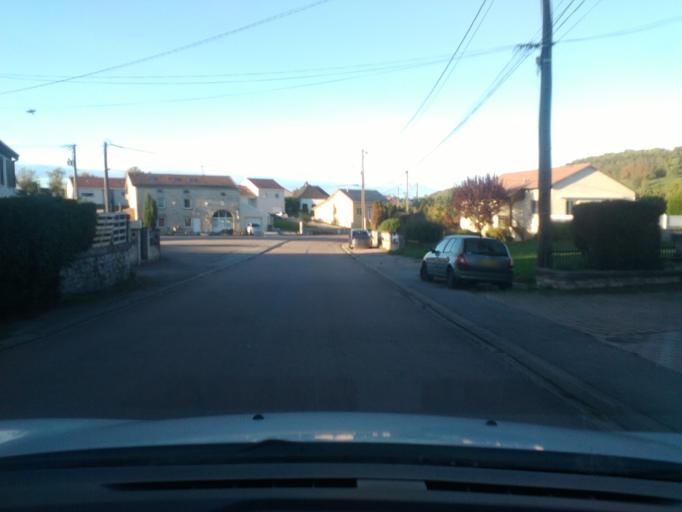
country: FR
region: Lorraine
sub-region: Departement des Vosges
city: Vincey
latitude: 48.3268
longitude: 6.2976
